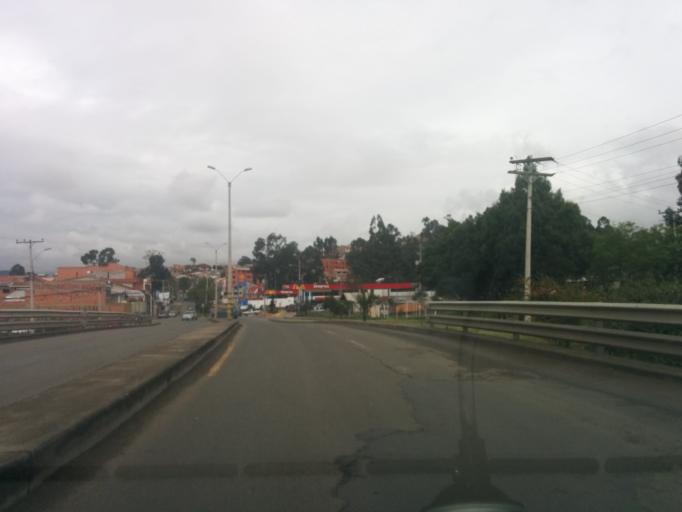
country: EC
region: Azuay
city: Cuenca
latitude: -2.8898
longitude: -78.9643
